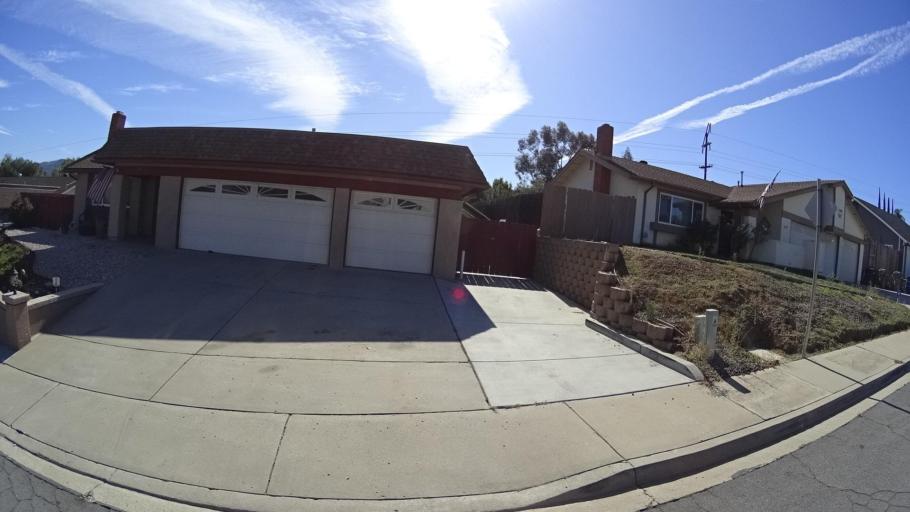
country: US
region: California
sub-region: San Diego County
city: Lakeside
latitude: 32.8381
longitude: -116.9121
